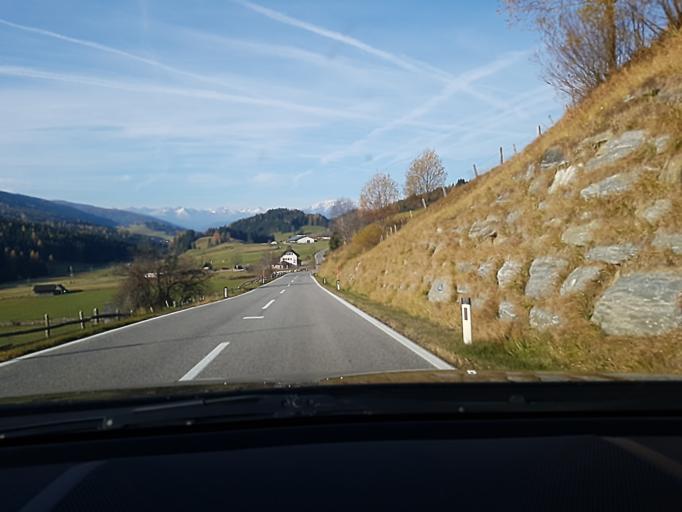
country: AT
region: Styria
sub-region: Politischer Bezirk Murau
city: Krakauschatten
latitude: 47.1440
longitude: 13.8965
